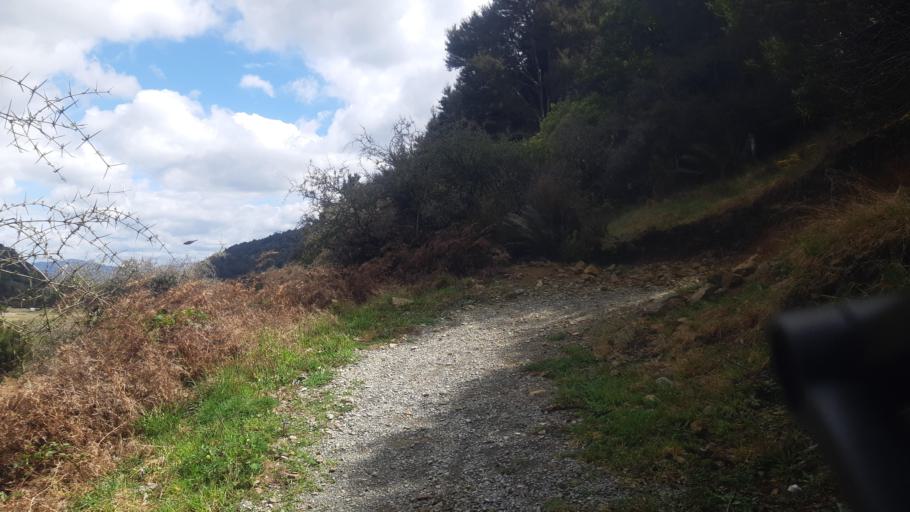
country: NZ
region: Tasman
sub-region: Tasman District
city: Wakefield
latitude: -41.7980
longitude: 172.8449
